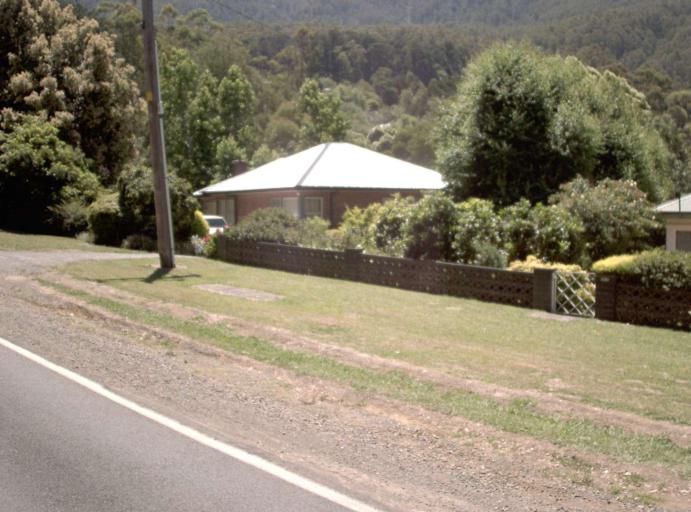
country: AU
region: Victoria
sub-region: Yarra Ranges
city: Millgrove
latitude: -37.7499
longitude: 145.7082
